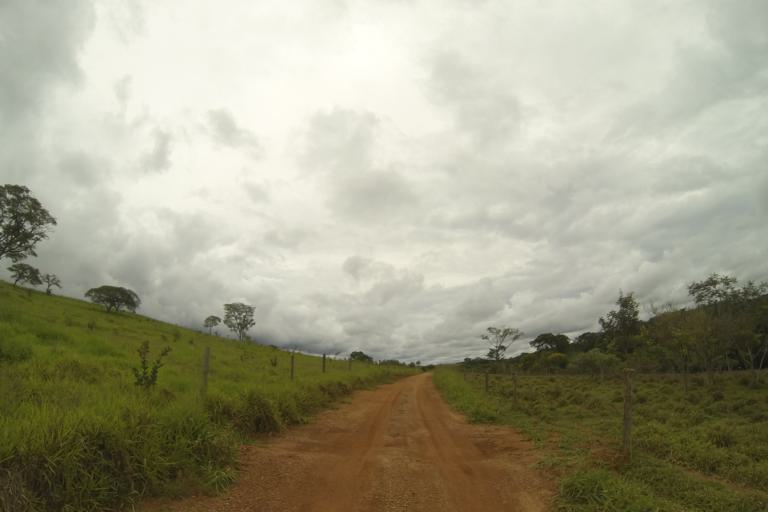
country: BR
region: Minas Gerais
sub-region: Ibia
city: Ibia
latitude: -19.7206
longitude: -46.5709
